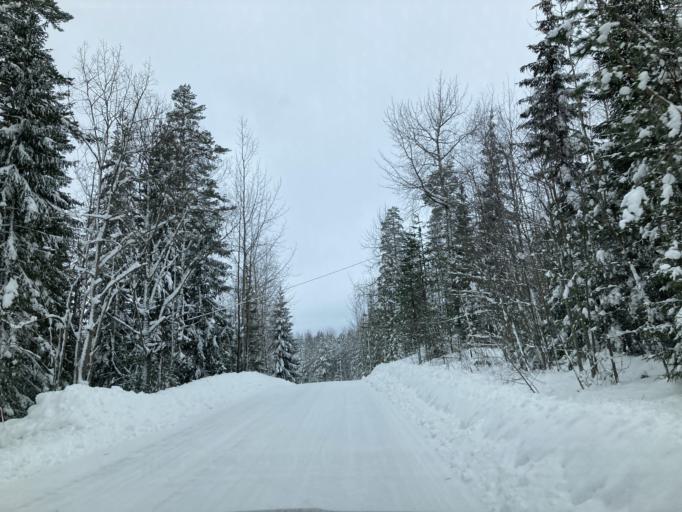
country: FI
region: Central Finland
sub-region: Jaemsae
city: Jaemsae
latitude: 61.8751
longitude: 25.3190
